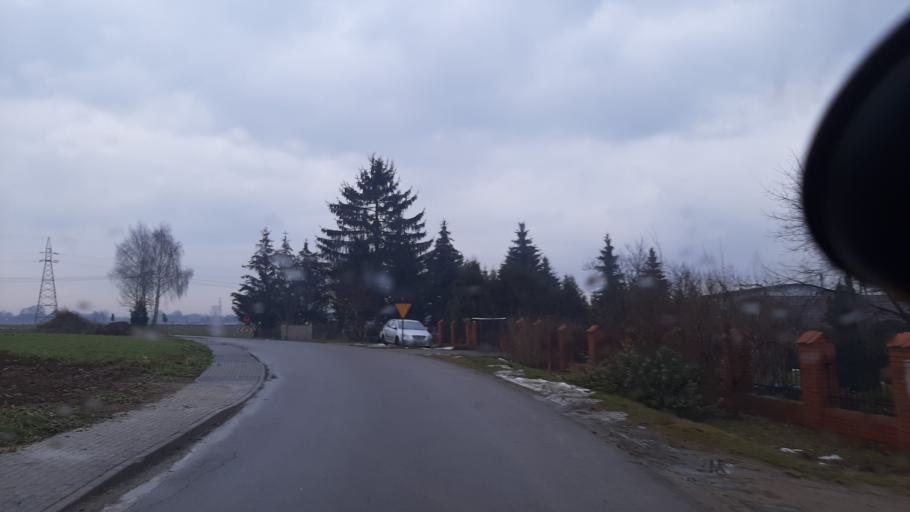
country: PL
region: Lublin Voivodeship
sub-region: Powiat lubelski
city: Niemce
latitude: 51.3187
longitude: 22.5893
